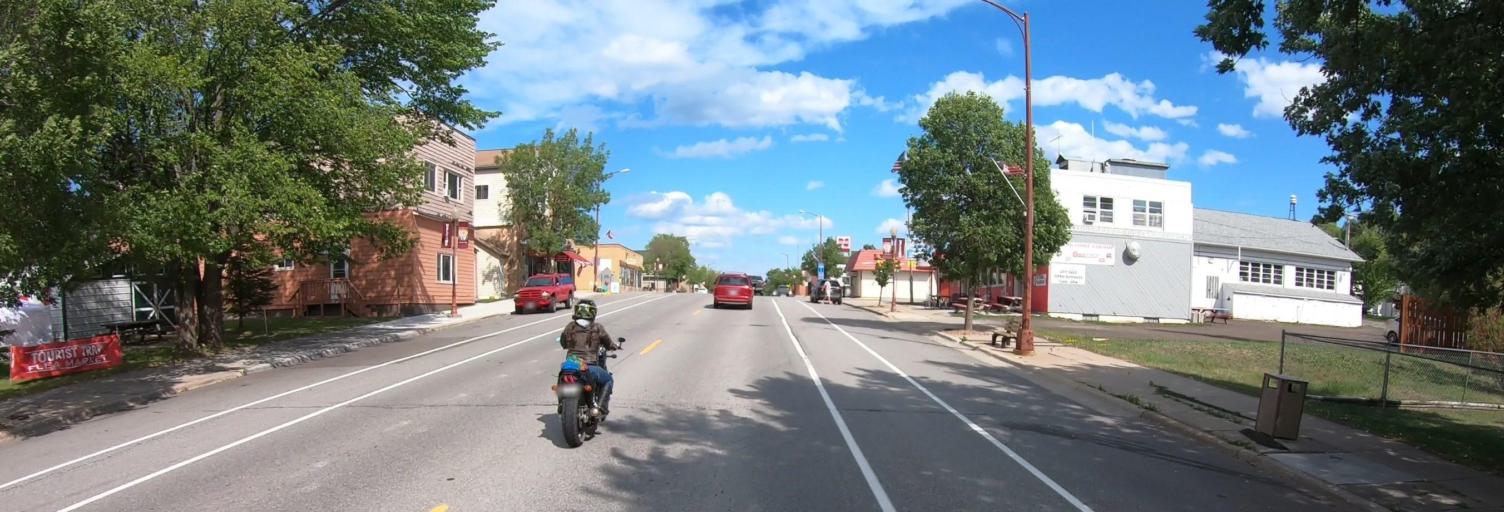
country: US
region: Minnesota
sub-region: Saint Louis County
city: Aurora
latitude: 47.8053
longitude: -92.2778
